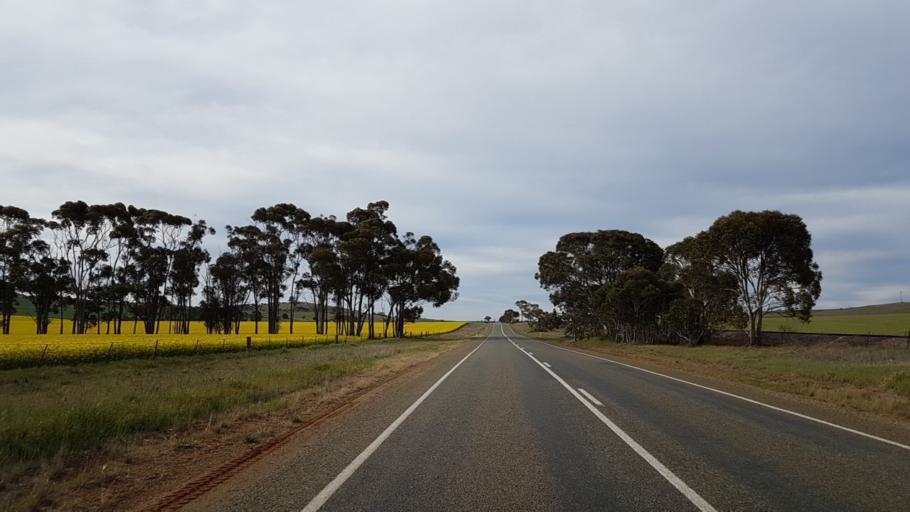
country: AU
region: South Australia
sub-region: Northern Areas
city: Jamestown
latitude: -33.1494
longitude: 138.6153
